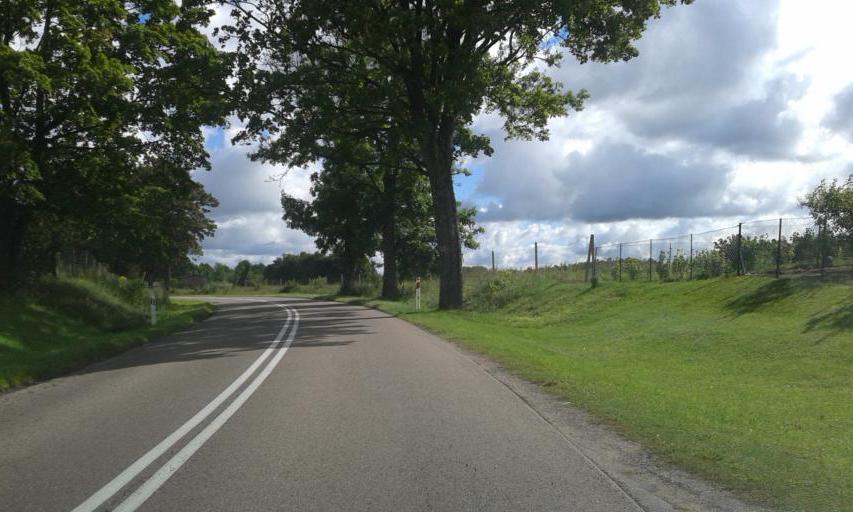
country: PL
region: West Pomeranian Voivodeship
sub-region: Powiat koszalinski
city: Bobolice
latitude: 53.9736
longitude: 16.6610
